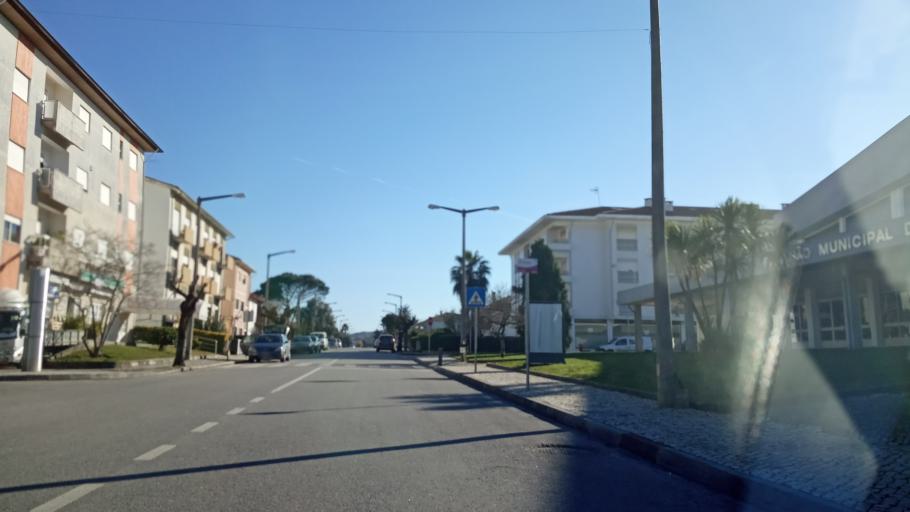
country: PT
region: Aveiro
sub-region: Anadia
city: Anadia
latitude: 40.4391
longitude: -8.4355
